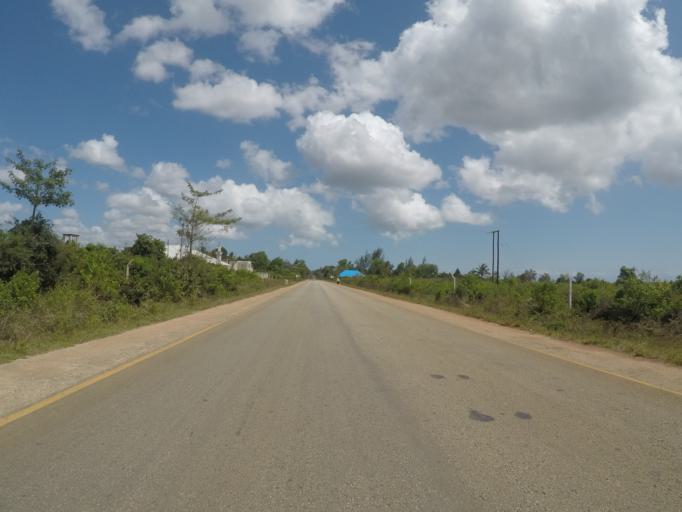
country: TZ
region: Zanzibar Central/South
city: Koani
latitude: -6.1609
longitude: 39.3299
